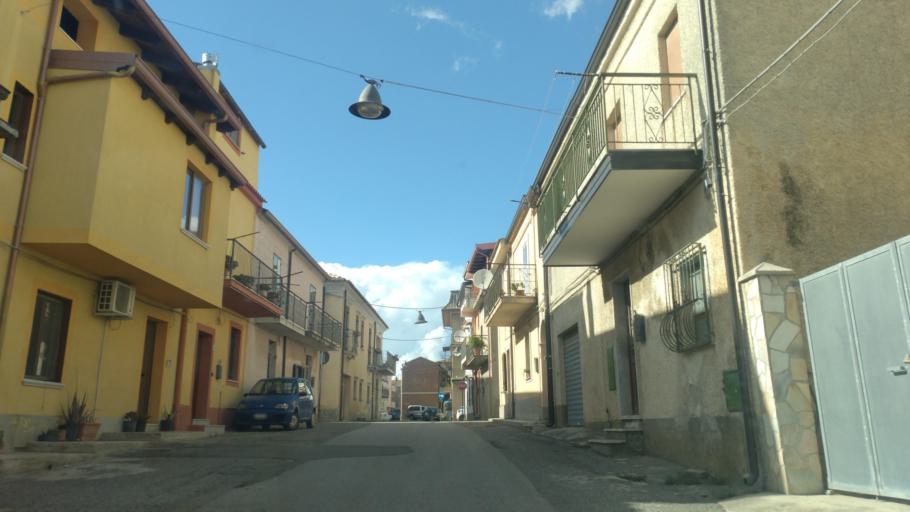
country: IT
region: Calabria
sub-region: Provincia di Catanzaro
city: Staletti
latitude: 38.7641
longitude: 16.5404
